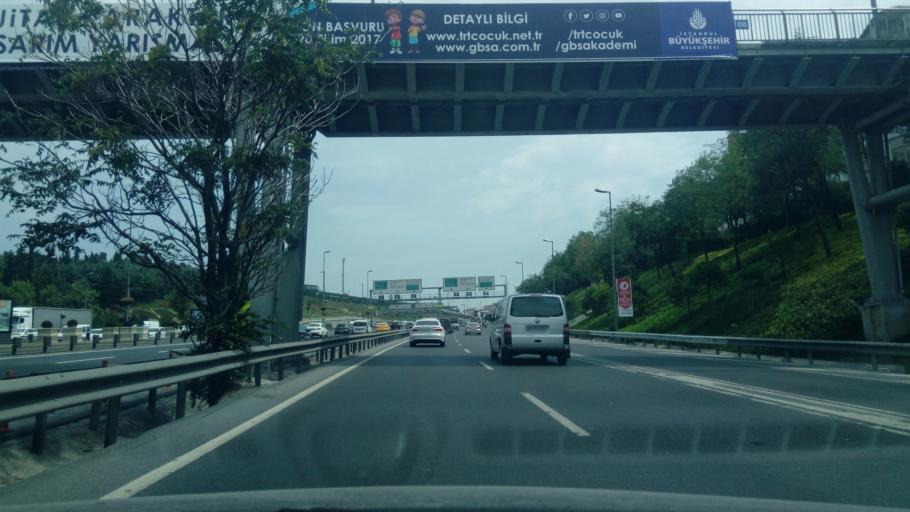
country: TR
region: Istanbul
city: Istanbul
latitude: 41.0476
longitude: 28.9456
